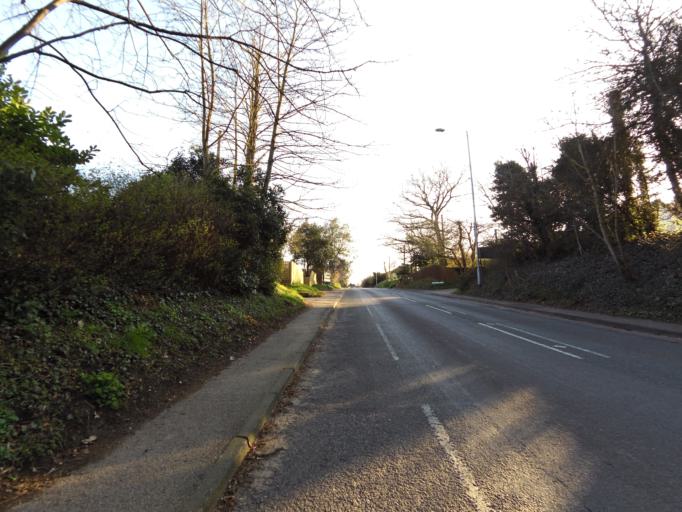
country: GB
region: England
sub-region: Suffolk
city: Woodbridge
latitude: 52.0760
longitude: 1.2844
